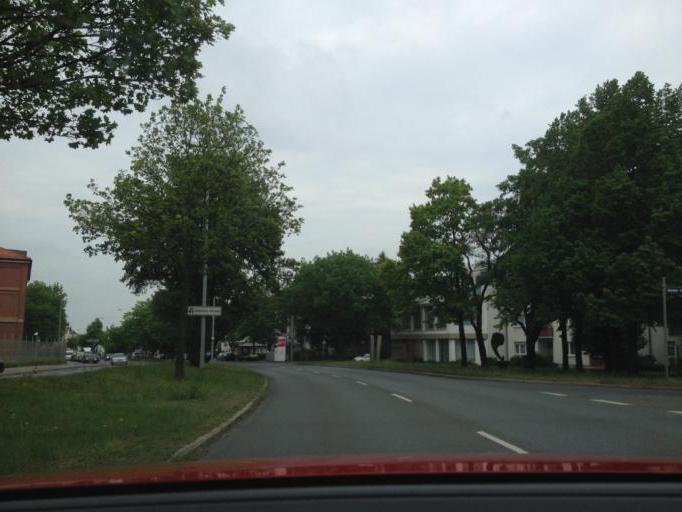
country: DE
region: Bavaria
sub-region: Regierungsbezirk Mittelfranken
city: Grossreuth bei Schweinau
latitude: 49.4357
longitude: 11.0385
